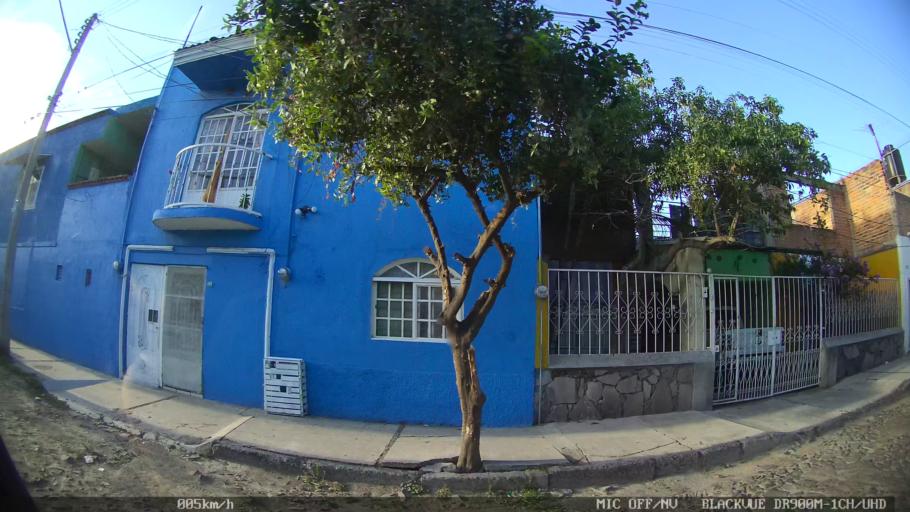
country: MX
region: Jalisco
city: Tlaquepaque
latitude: 20.7066
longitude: -103.3011
